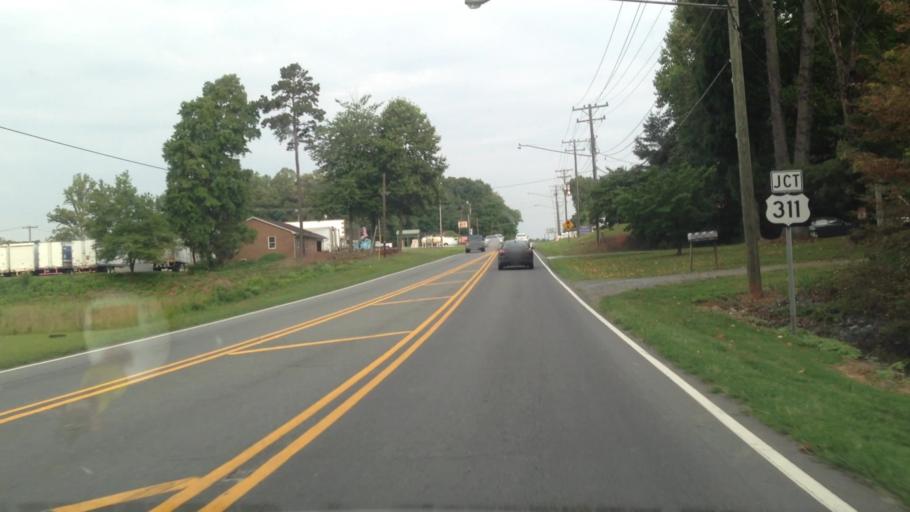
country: US
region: North Carolina
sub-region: Forsyth County
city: Walkertown
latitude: 36.1698
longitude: -80.1558
